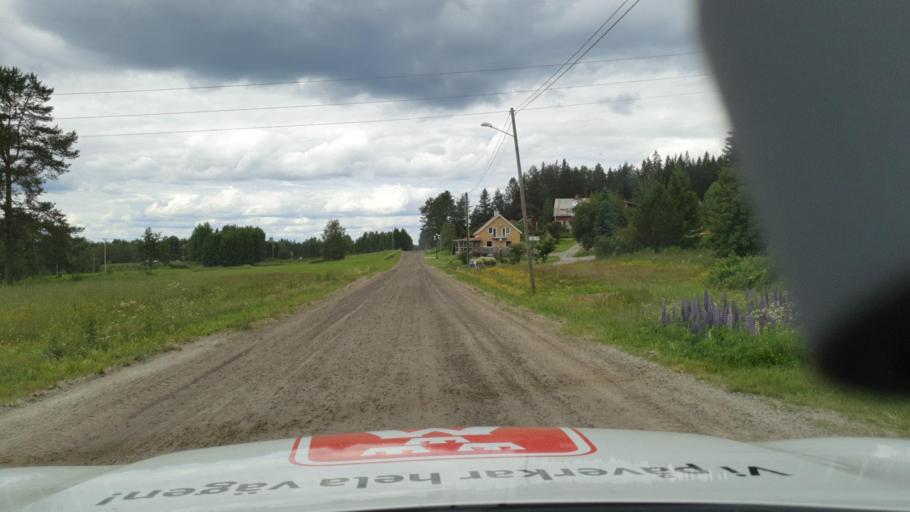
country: SE
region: Vaesterbotten
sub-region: Bjurholms Kommun
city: Bjurholm
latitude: 63.8187
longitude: 19.0266
